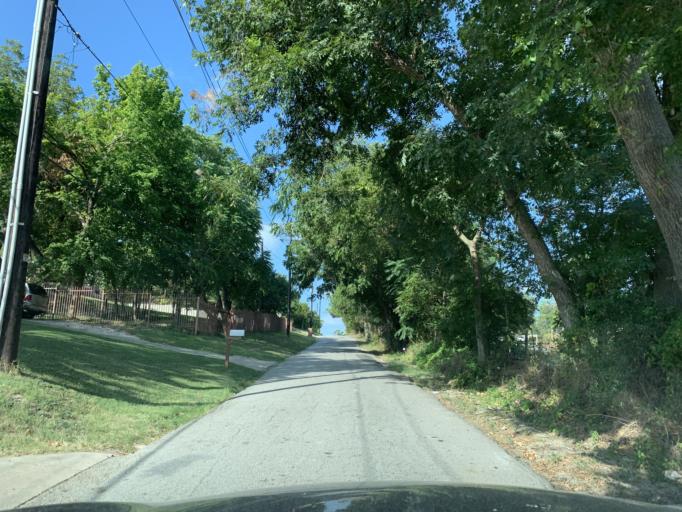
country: US
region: Texas
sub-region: Dallas County
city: Hutchins
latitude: 32.6768
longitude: -96.7832
